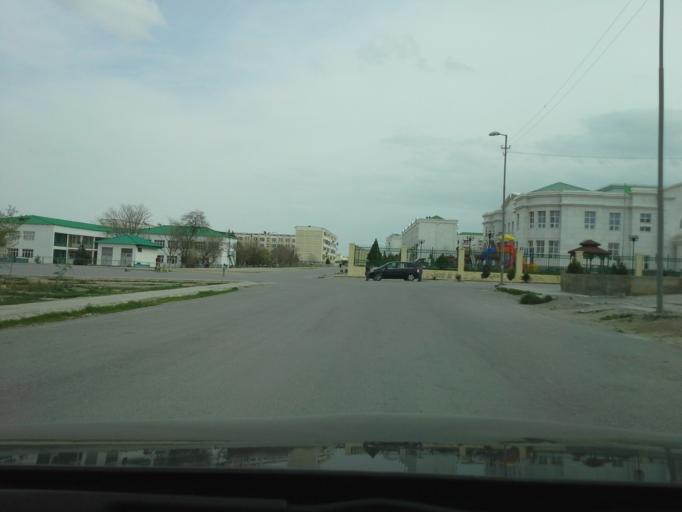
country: TM
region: Ahal
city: Abadan
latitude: 38.0539
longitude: 58.1400
